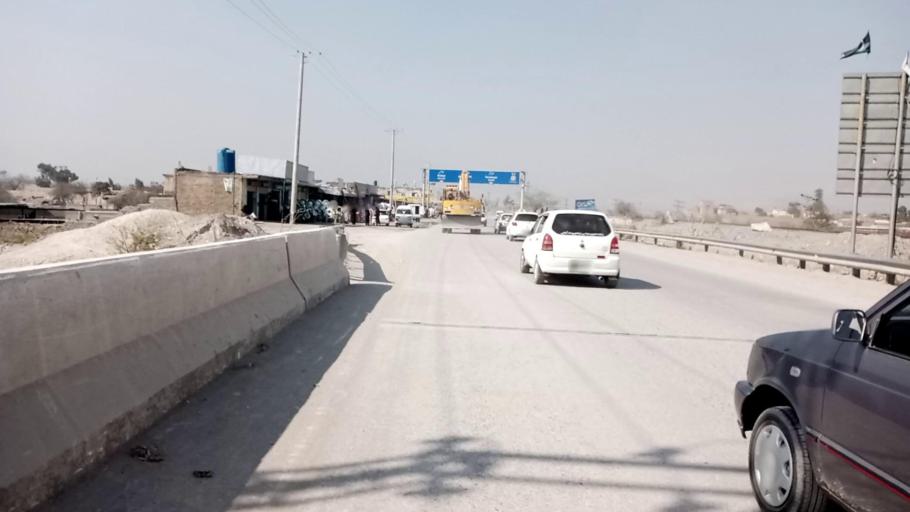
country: PK
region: Khyber Pakhtunkhwa
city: Peshawar
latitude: 33.9998
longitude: 71.4004
